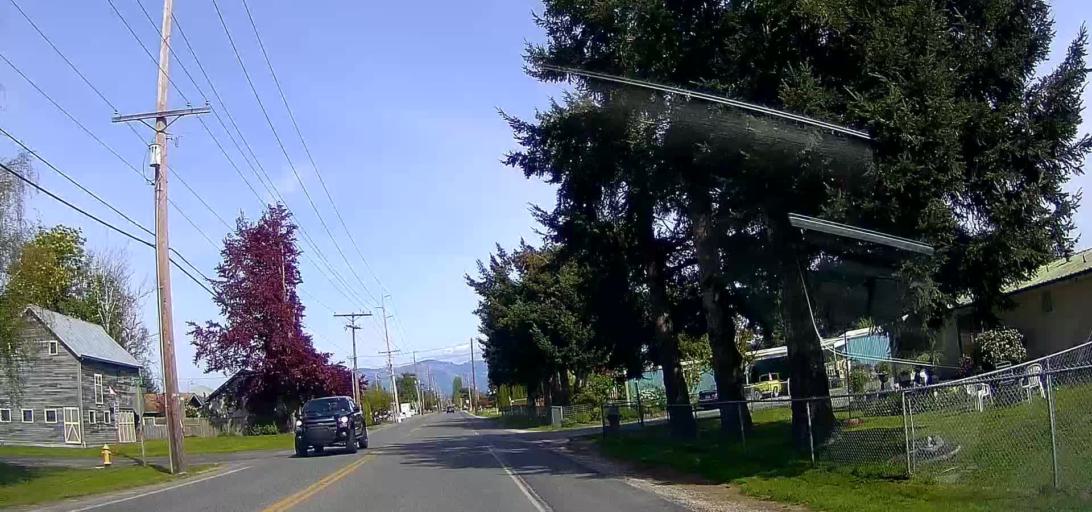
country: US
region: Washington
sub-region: Skagit County
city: Mount Vernon
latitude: 48.4209
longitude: -122.3992
